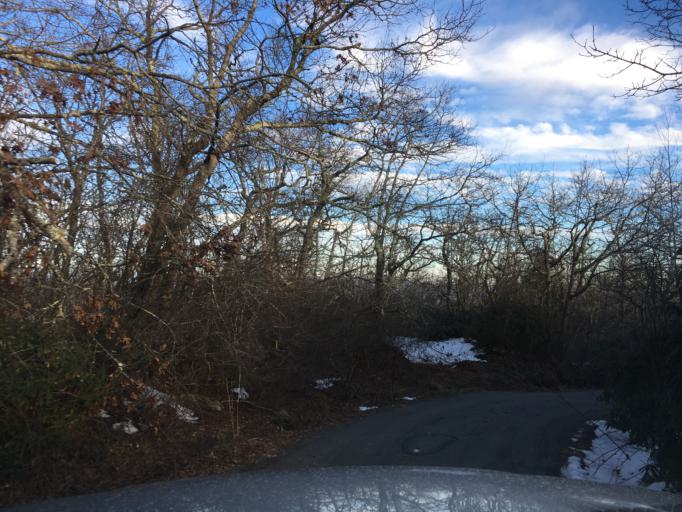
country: US
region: North Carolina
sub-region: Jackson County
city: Cullowhee
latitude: 35.1315
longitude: -82.9823
